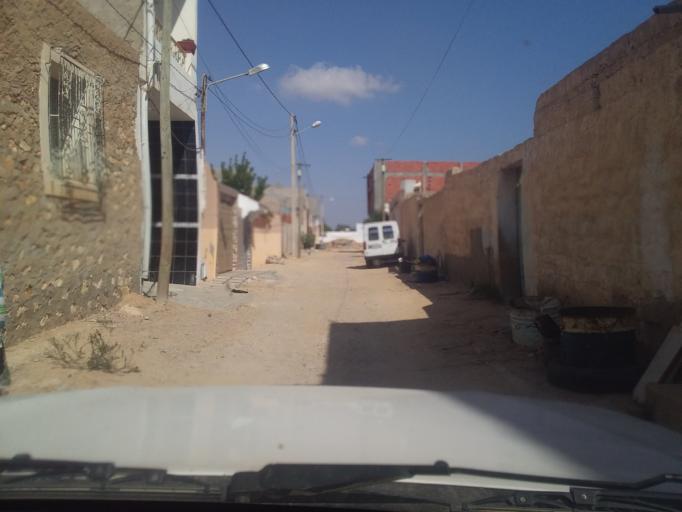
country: TN
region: Qabis
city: Gabes
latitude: 33.6255
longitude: 10.2814
